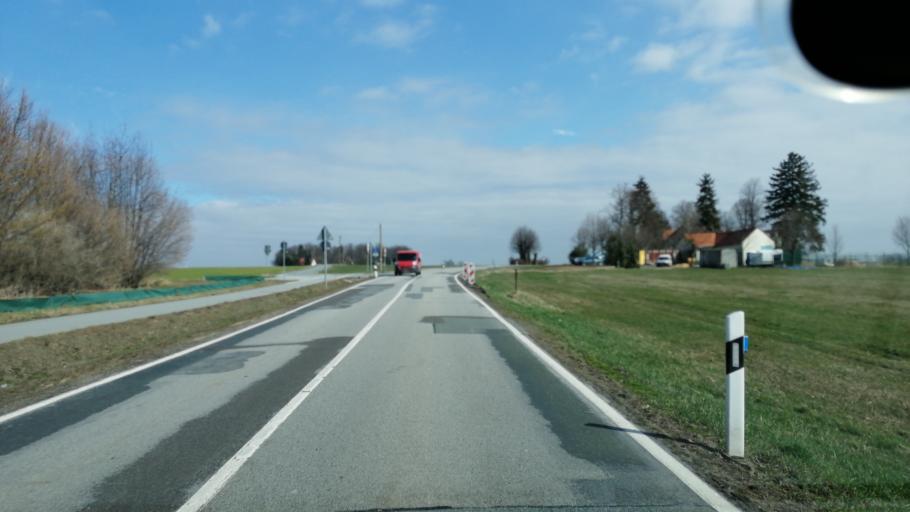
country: DE
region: Saxony
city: Grossschweidnitz
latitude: 51.0851
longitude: 14.6334
